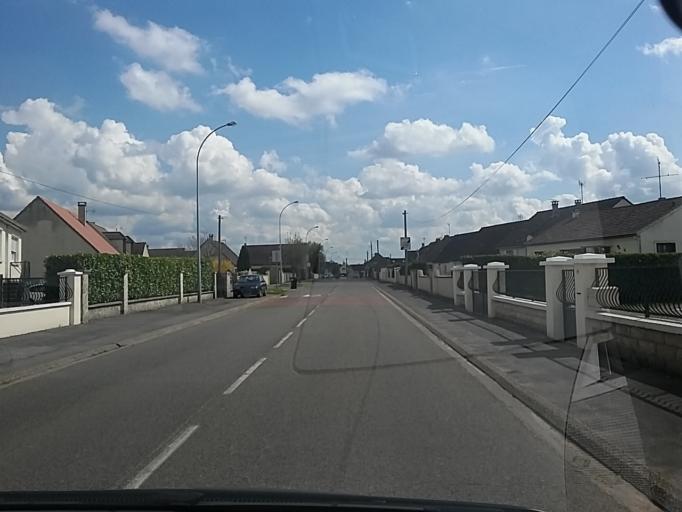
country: FR
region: Picardie
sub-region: Departement de l'Oise
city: Chevrieres
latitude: 49.3464
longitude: 2.6683
